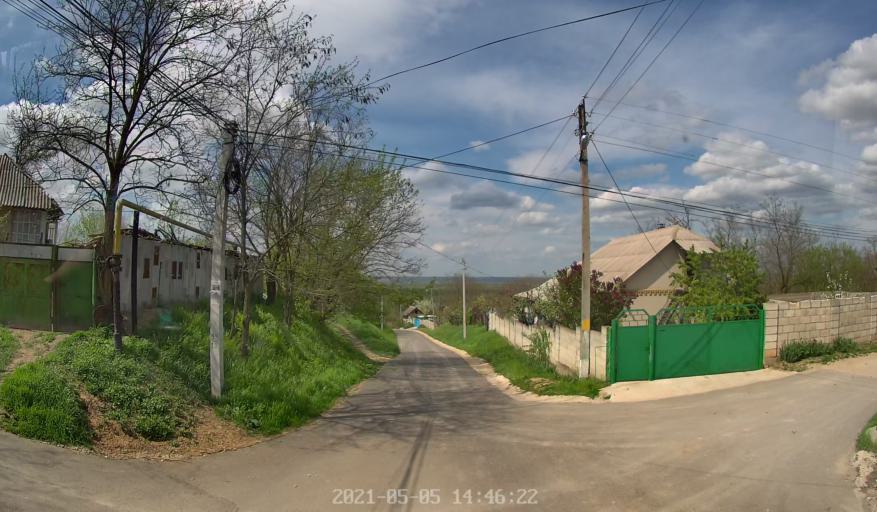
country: MD
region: Chisinau
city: Vadul lui Voda
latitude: 47.0934
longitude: 29.1732
